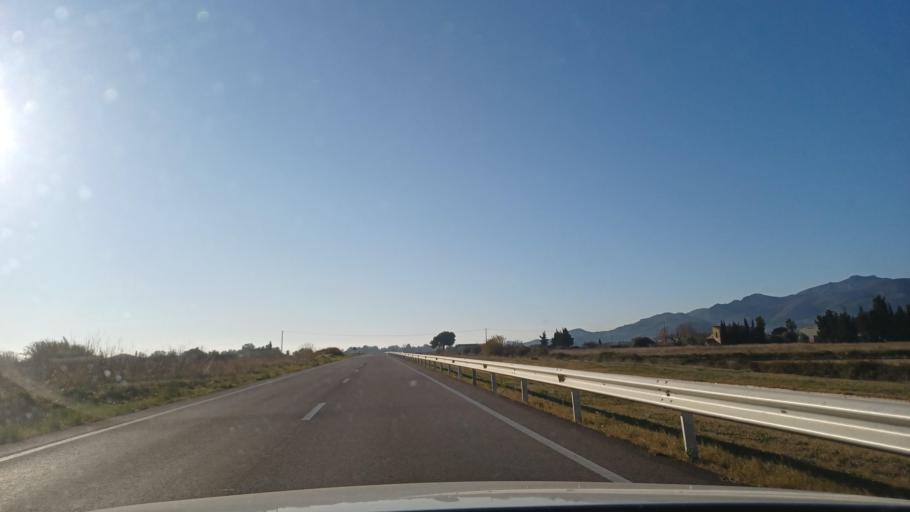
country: ES
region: Catalonia
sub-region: Provincia de Tarragona
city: Amposta
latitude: 40.6955
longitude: 0.5895
